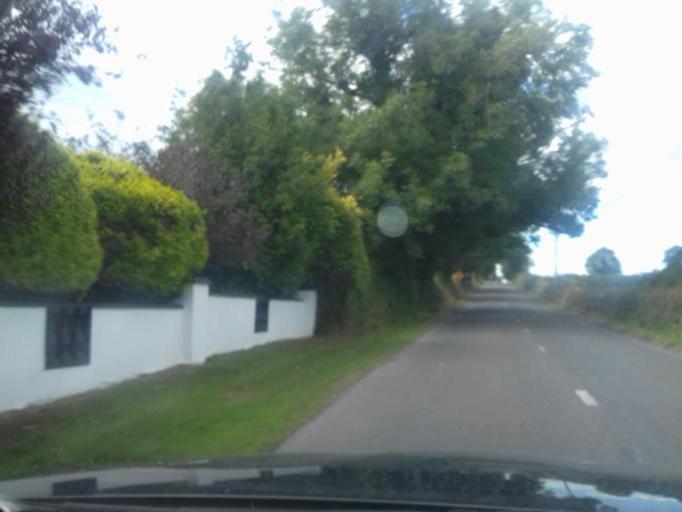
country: IE
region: Munster
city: Carrick-on-Suir
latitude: 52.2837
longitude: -7.4495
